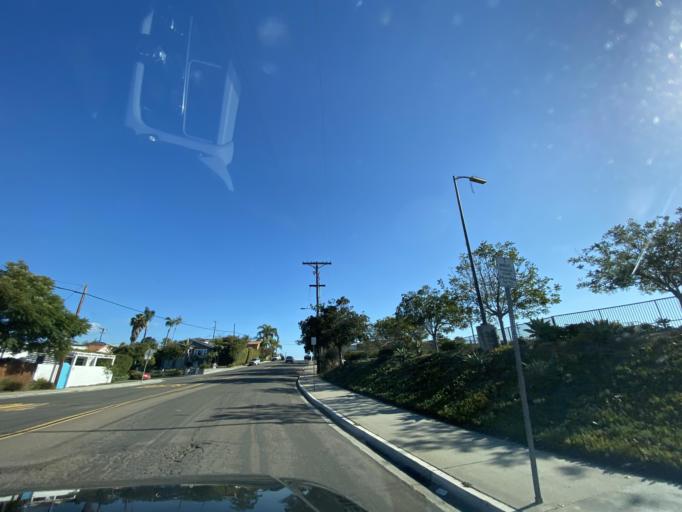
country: US
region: California
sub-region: San Diego County
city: Coronado
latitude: 32.7334
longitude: -117.2323
